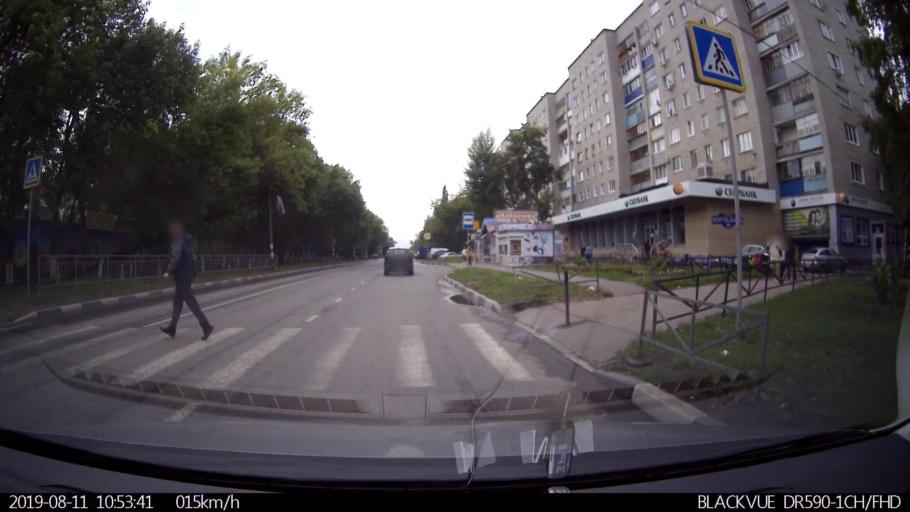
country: RU
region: Ulyanovsk
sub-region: Ulyanovskiy Rayon
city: Ulyanovsk
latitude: 54.2593
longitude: 48.3342
